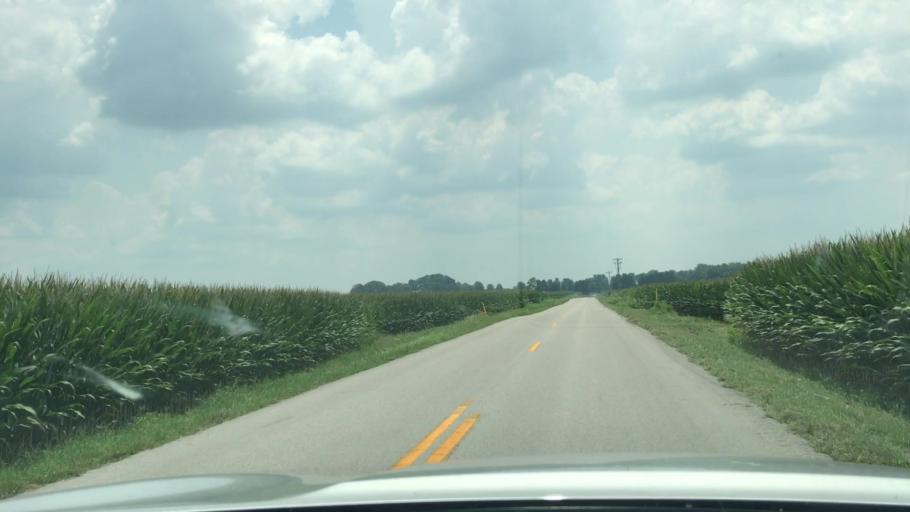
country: US
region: Kentucky
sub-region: Todd County
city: Elkton
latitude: 36.7504
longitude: -87.0962
